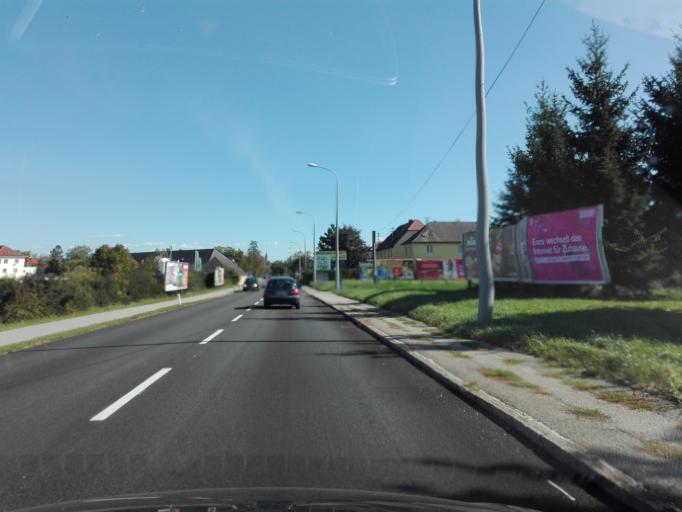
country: AT
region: Upper Austria
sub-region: Politischer Bezirk Linz-Land
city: Enns
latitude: 48.2165
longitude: 14.4516
